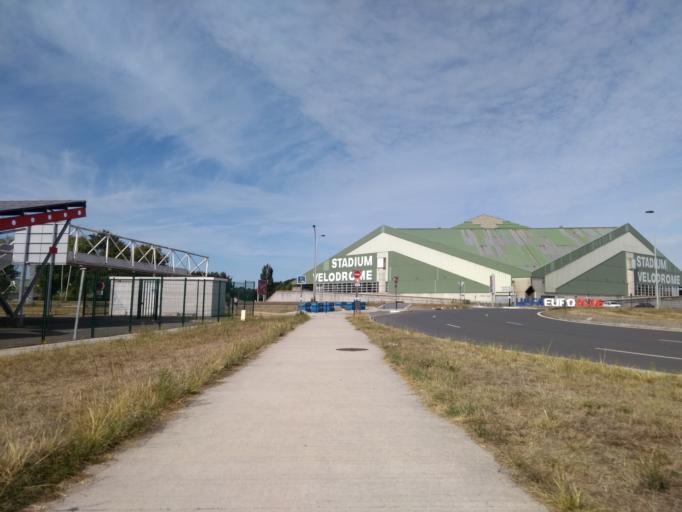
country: FR
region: Aquitaine
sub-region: Departement de la Gironde
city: Le Bouscat
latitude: 44.8973
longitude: -0.5661
